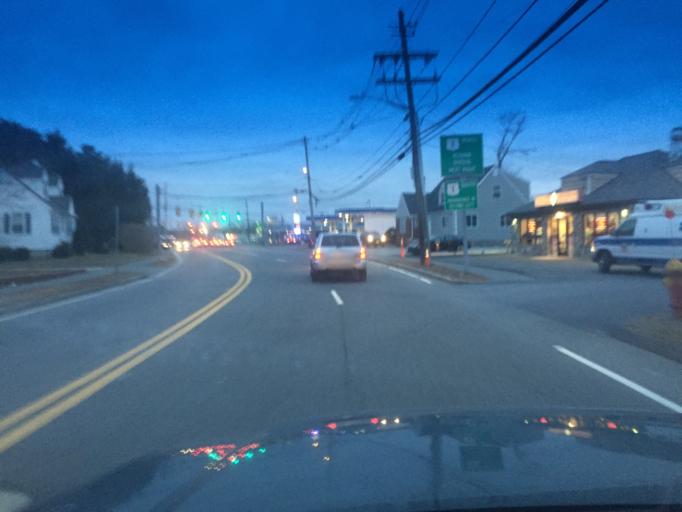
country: US
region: Massachusetts
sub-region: Norfolk County
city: Norwood
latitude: 42.1789
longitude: -71.1886
